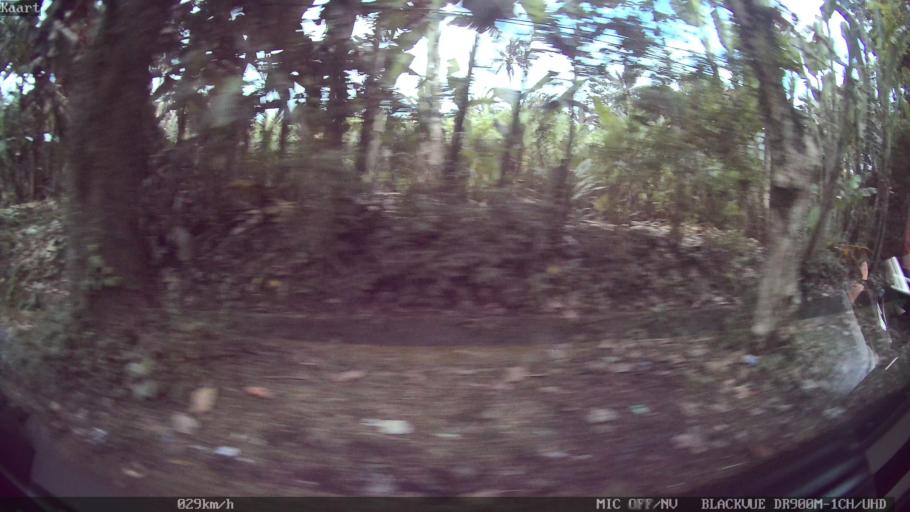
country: ID
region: Bali
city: Banjar Batur
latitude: -8.5927
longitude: 115.2097
